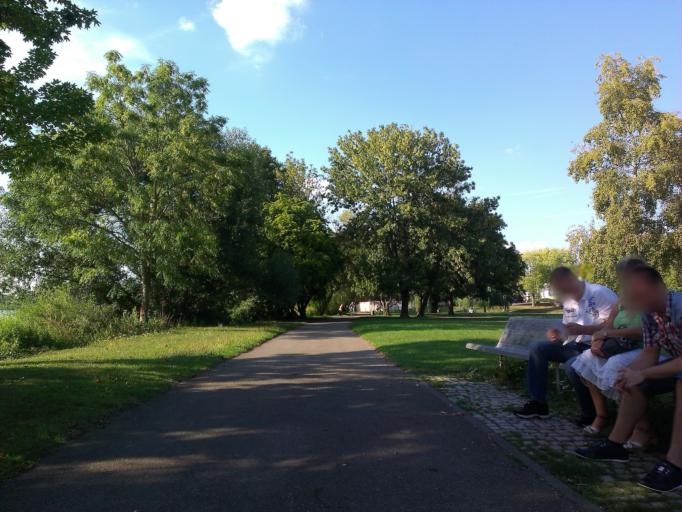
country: DE
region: Baden-Wuerttemberg
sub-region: Karlsruhe Region
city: Ladenburg
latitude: 49.4668
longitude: 8.6055
